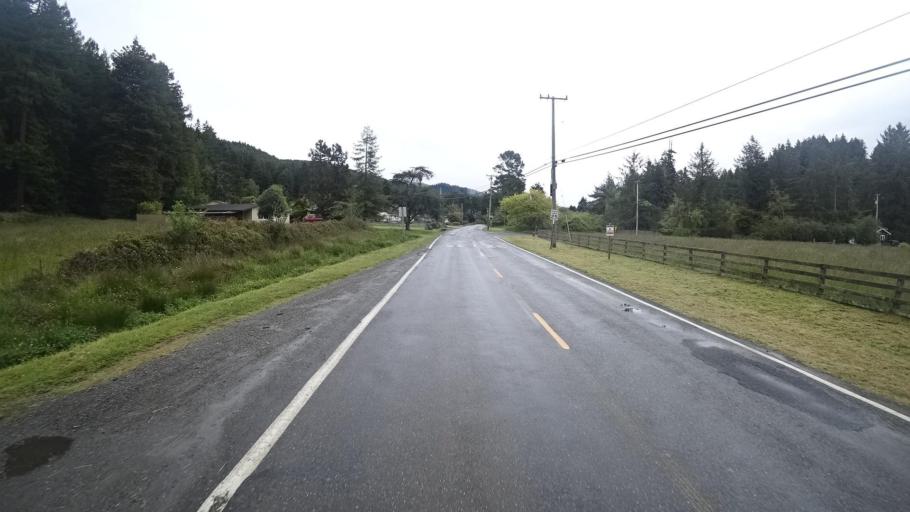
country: US
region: California
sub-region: Humboldt County
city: Bayside
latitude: 40.8331
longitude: -124.0439
